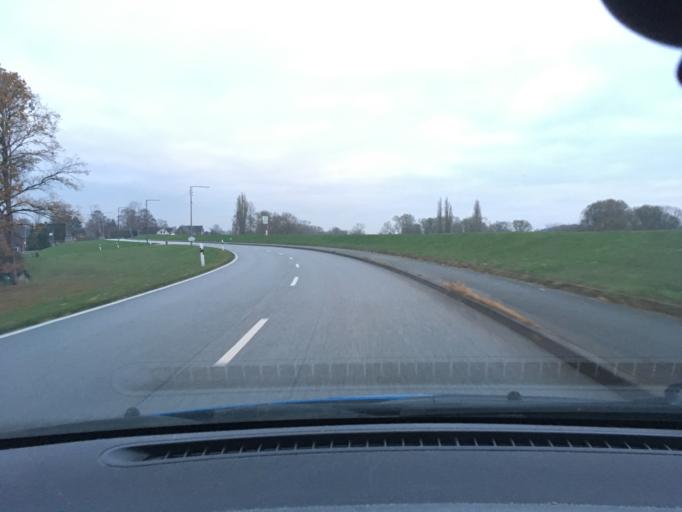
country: DE
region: Lower Saxony
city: Winsen
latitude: 53.4003
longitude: 10.2081
